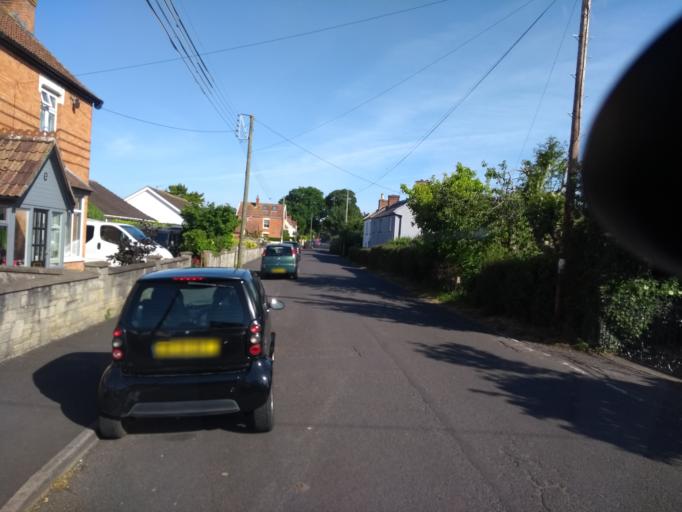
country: GB
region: England
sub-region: Somerset
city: Highbridge
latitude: 51.2480
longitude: -2.9522
